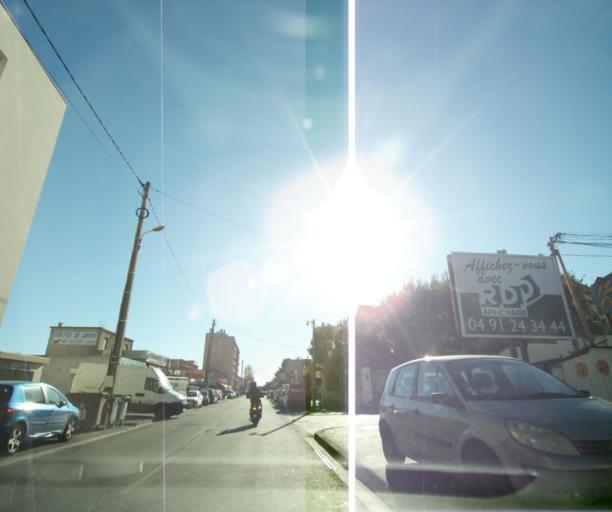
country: FR
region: Provence-Alpes-Cote d'Azur
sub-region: Departement des Bouches-du-Rhone
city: Marseille 15
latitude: 43.3813
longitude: 5.3577
